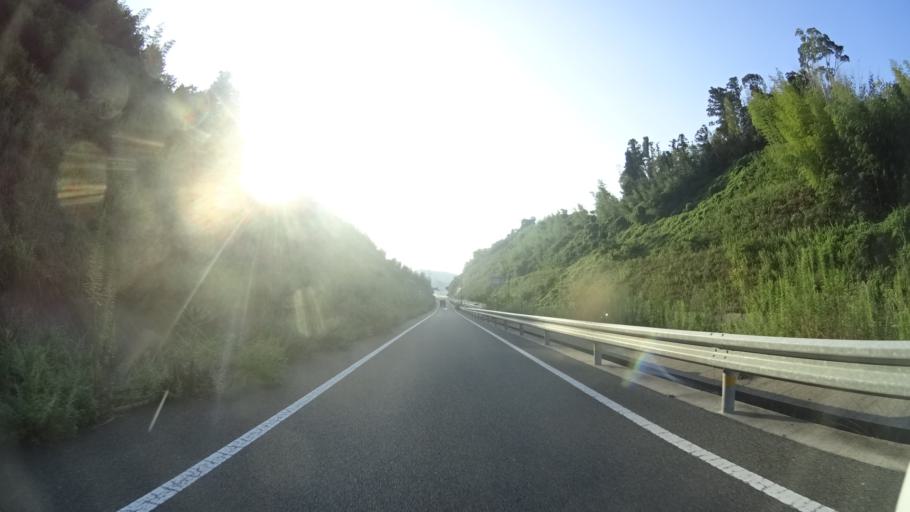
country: JP
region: Yamaguchi
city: Hagi
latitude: 34.3858
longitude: 131.3473
